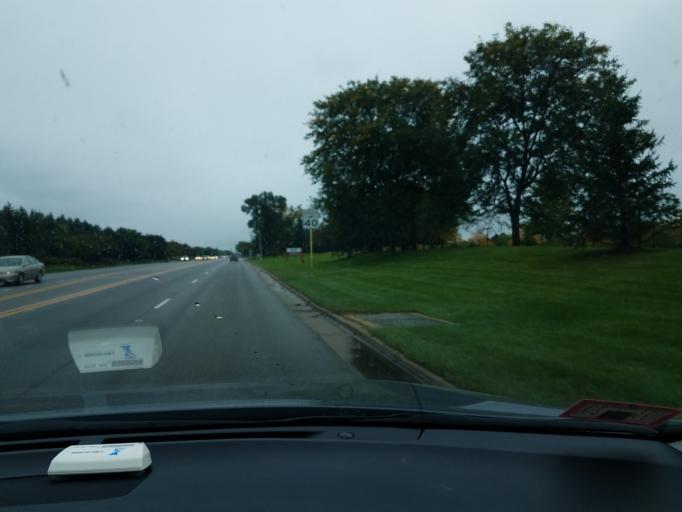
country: US
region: Illinois
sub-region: Lake County
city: Lincolnshire
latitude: 42.1874
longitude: -87.9283
